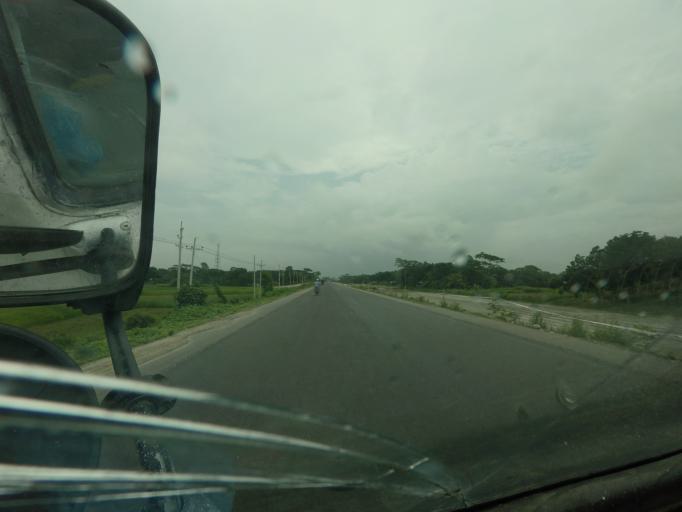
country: BD
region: Dhaka
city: Char Bhadrasan
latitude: 23.3766
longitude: 90.0184
